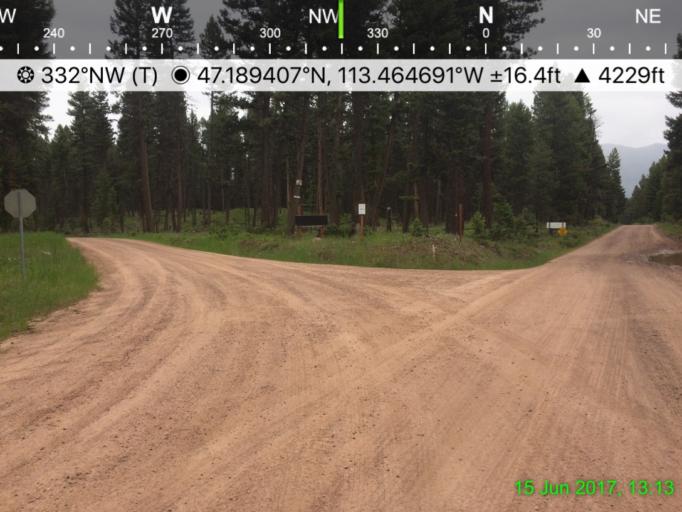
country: US
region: Montana
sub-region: Missoula County
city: Seeley Lake
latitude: 47.1894
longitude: -113.4647
